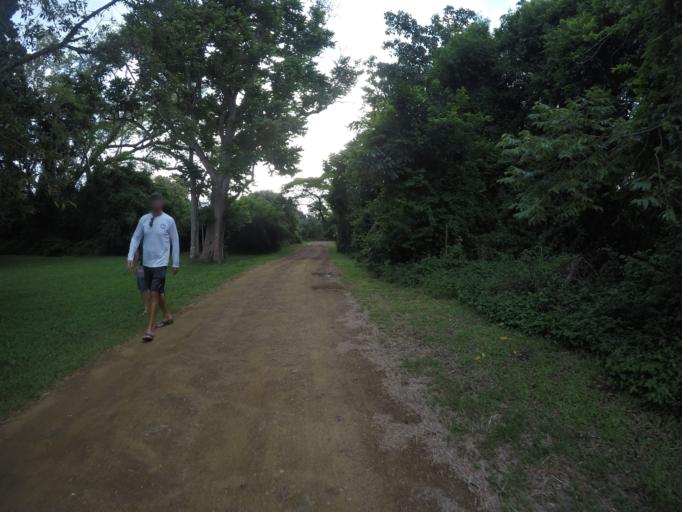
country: ZA
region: KwaZulu-Natal
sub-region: uMkhanyakude District Municipality
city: Mtubatuba
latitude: -28.3882
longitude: 32.4076
